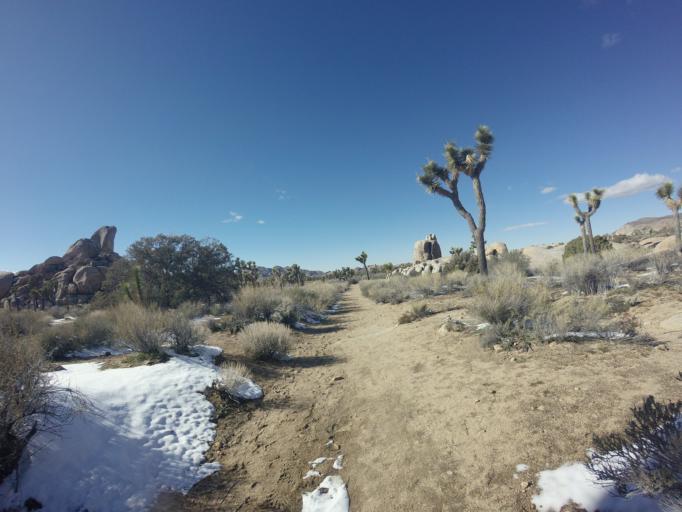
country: US
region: California
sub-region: San Bernardino County
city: Twentynine Palms
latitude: 33.9843
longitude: -116.1509
